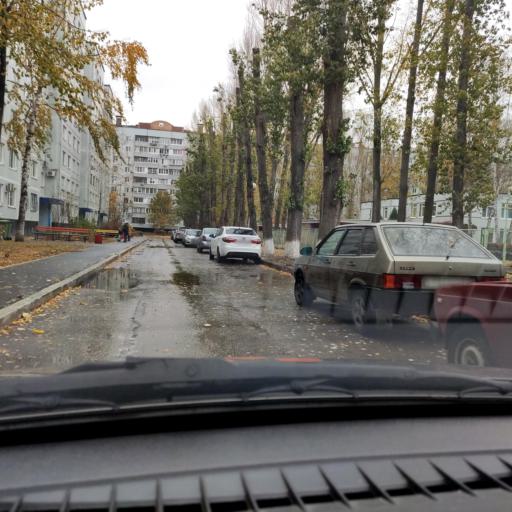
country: RU
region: Samara
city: Tol'yatti
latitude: 53.5114
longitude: 49.2944
